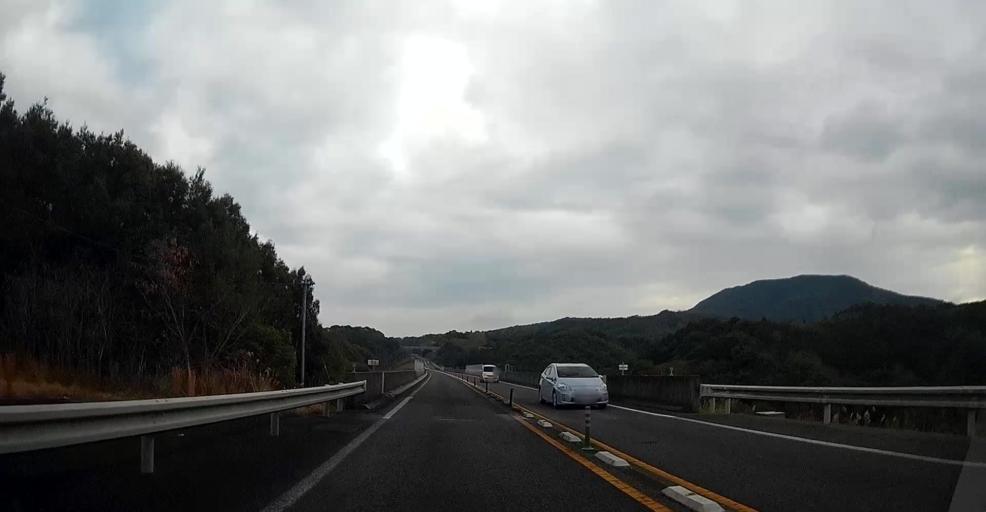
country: JP
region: Kumamoto
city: Hondo
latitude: 32.5080
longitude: 130.3390
